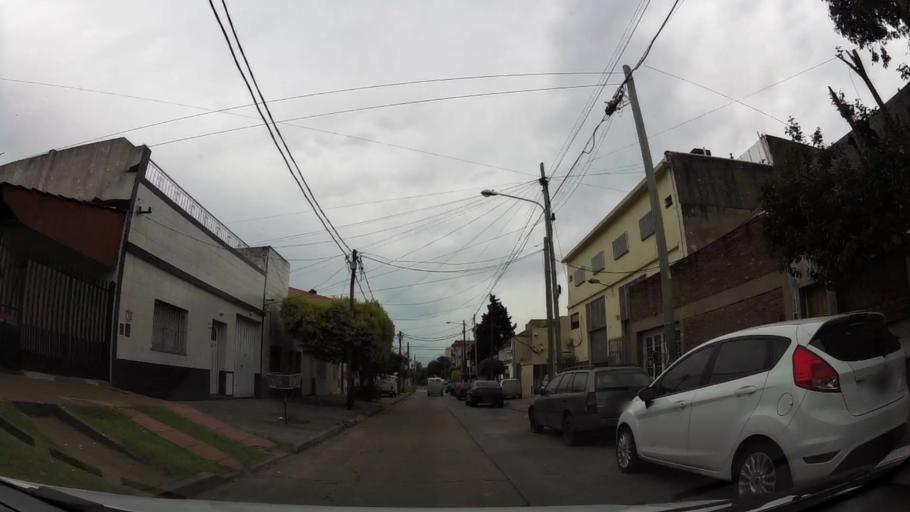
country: AR
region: Buenos Aires
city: San Justo
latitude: -34.6649
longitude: -58.5169
